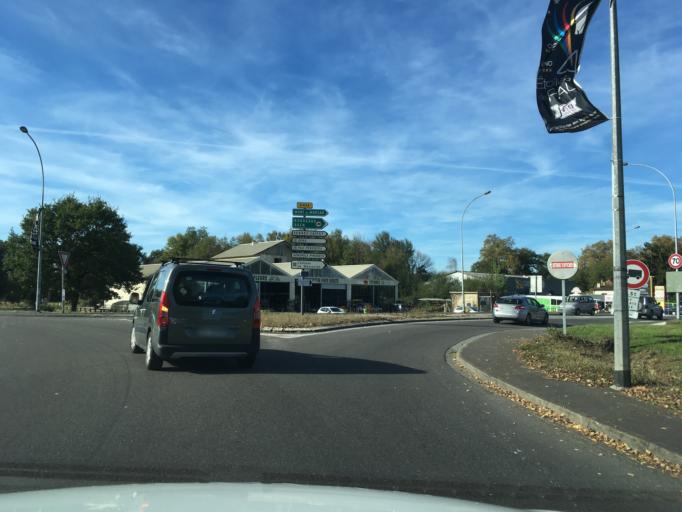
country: FR
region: Aquitaine
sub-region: Departement des Pyrenees-Atlantiques
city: Lons
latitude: 43.3387
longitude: -0.3796
